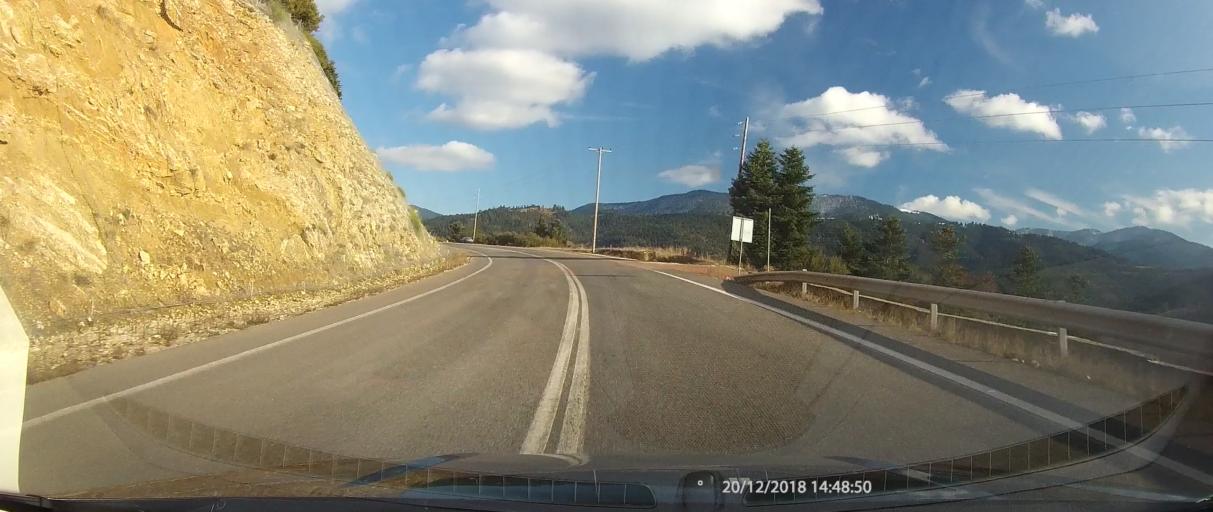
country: GR
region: Central Greece
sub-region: Nomos Evrytanias
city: Karpenisi
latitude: 38.9023
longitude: 21.7955
